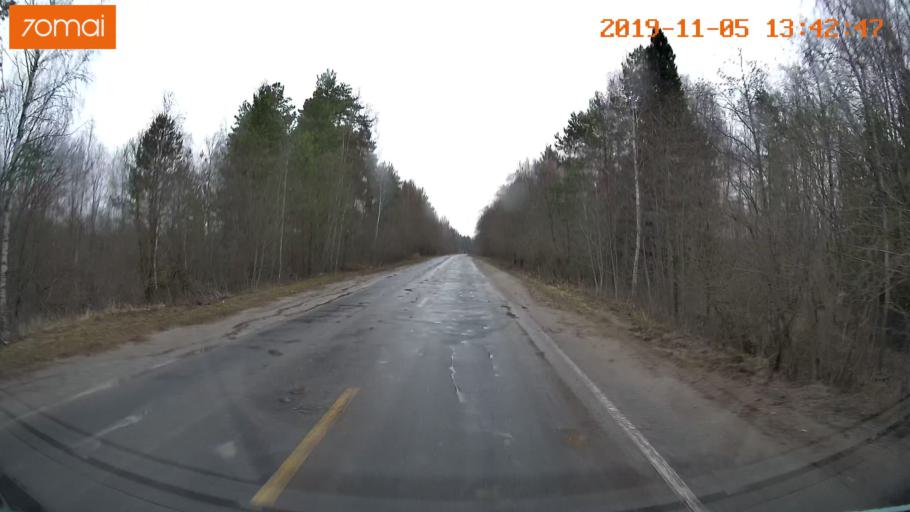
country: RU
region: Ivanovo
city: Shuya
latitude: 56.9689
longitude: 41.3978
